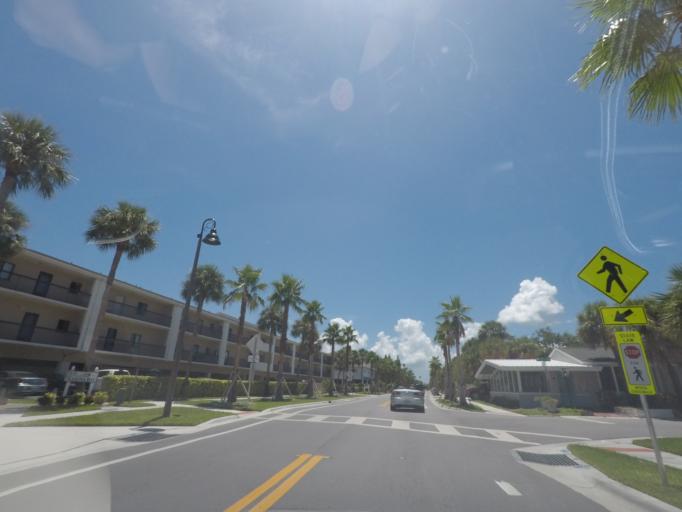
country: US
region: Florida
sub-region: Pinellas County
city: Saint Pete Beach
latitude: 27.7068
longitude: -82.7364
